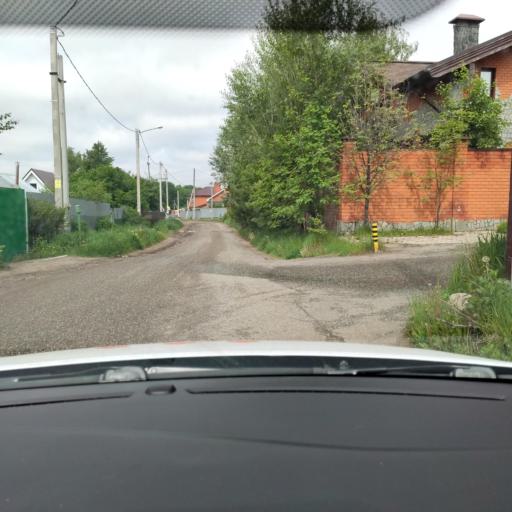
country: RU
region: Tatarstan
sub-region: Gorod Kazan'
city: Kazan
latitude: 55.8225
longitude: 49.2231
